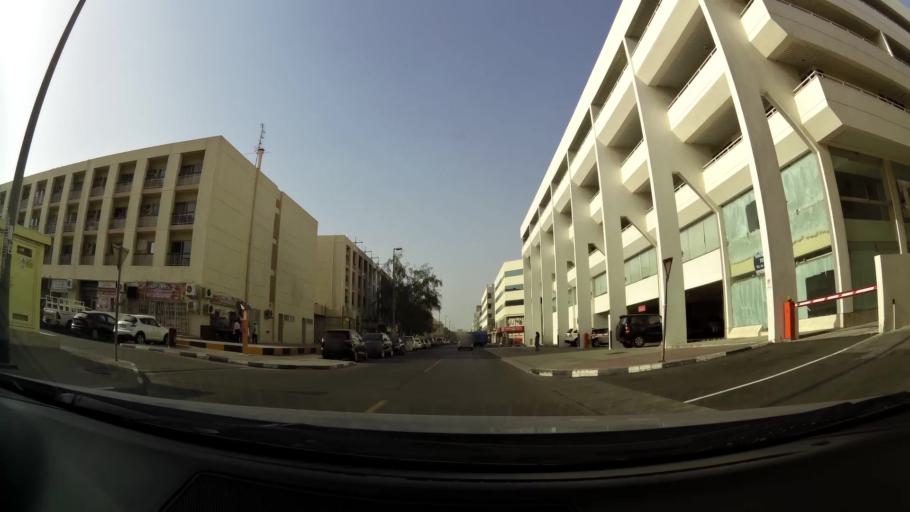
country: AE
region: Ash Shariqah
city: Sharjah
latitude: 25.2375
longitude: 55.3041
